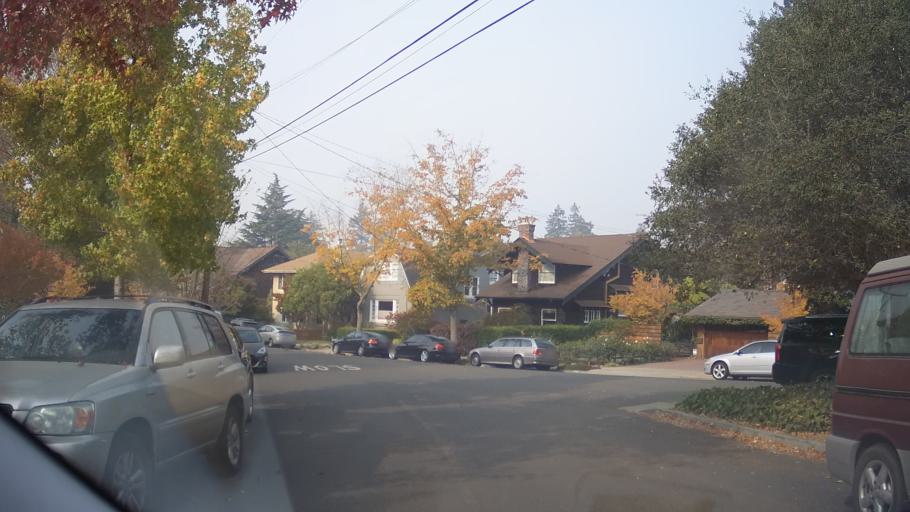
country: US
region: California
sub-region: Alameda County
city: Piedmont
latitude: 37.8541
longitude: -122.2425
